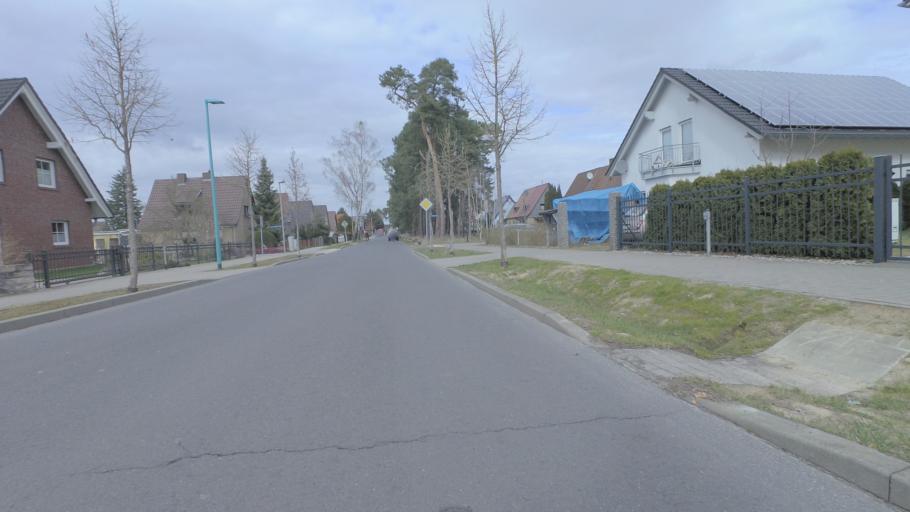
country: DE
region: Brandenburg
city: Ludwigsfelde
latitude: 52.2906
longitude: 13.2575
